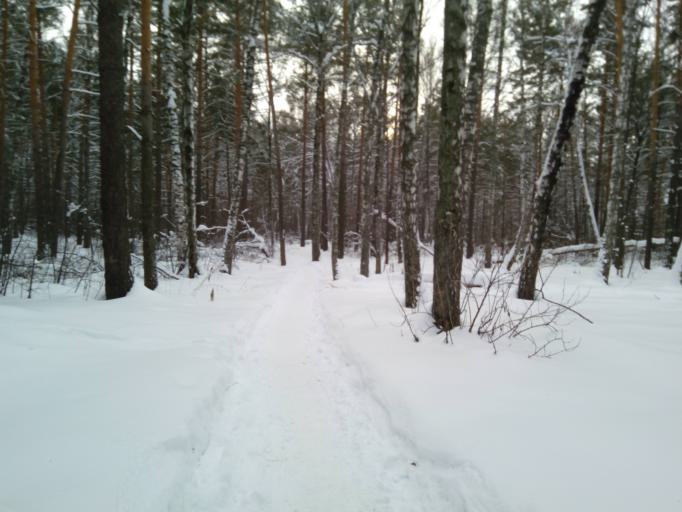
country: RU
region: Novosibirsk
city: Akademgorodok
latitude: 54.8592
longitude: 83.0929
